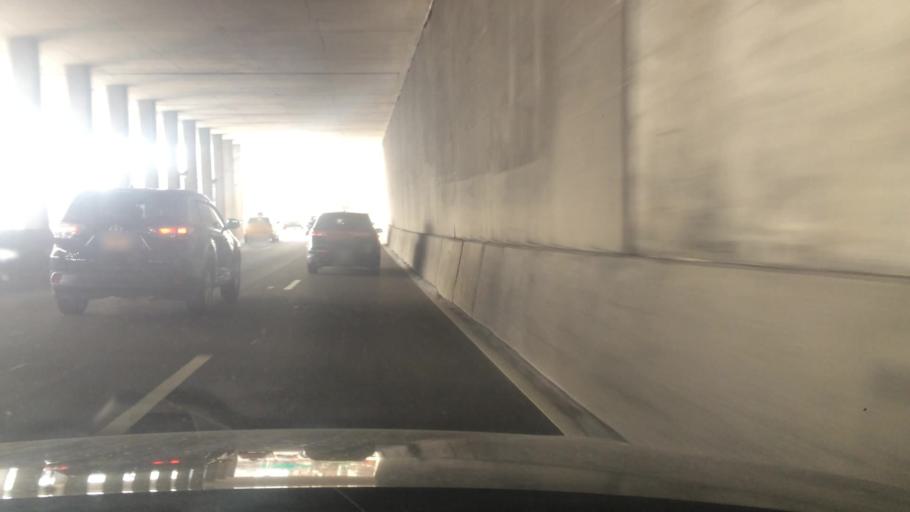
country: US
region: New York
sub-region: Queens County
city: Long Island City
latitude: 40.7559
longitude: -73.9610
